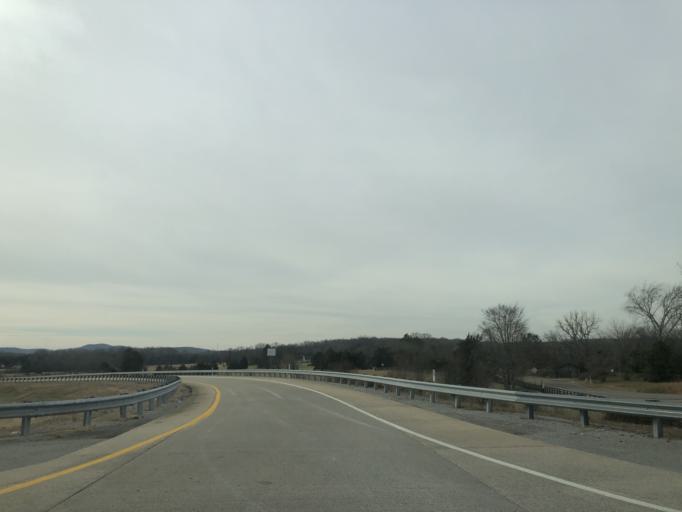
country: US
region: Tennessee
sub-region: Rutherford County
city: Smyrna
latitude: 35.8687
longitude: -86.5117
